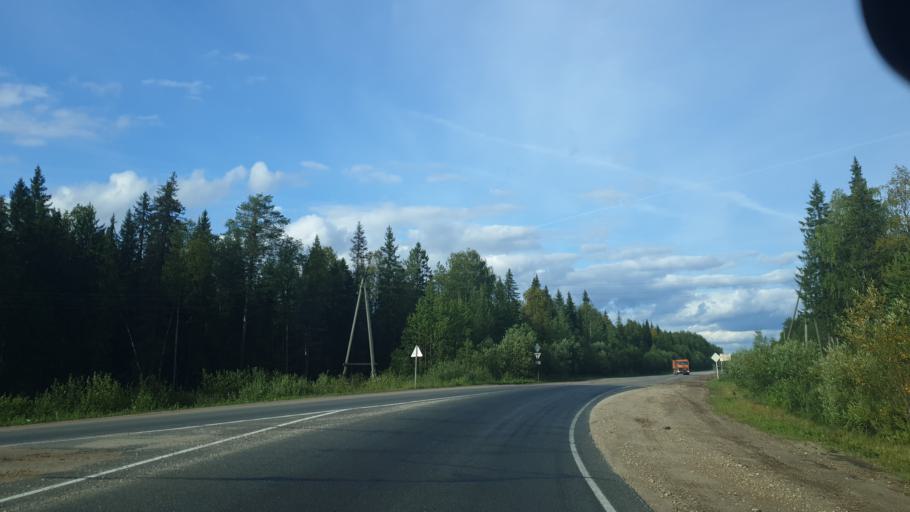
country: RU
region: Komi Republic
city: Ezhva
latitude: 61.7006
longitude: 50.6710
